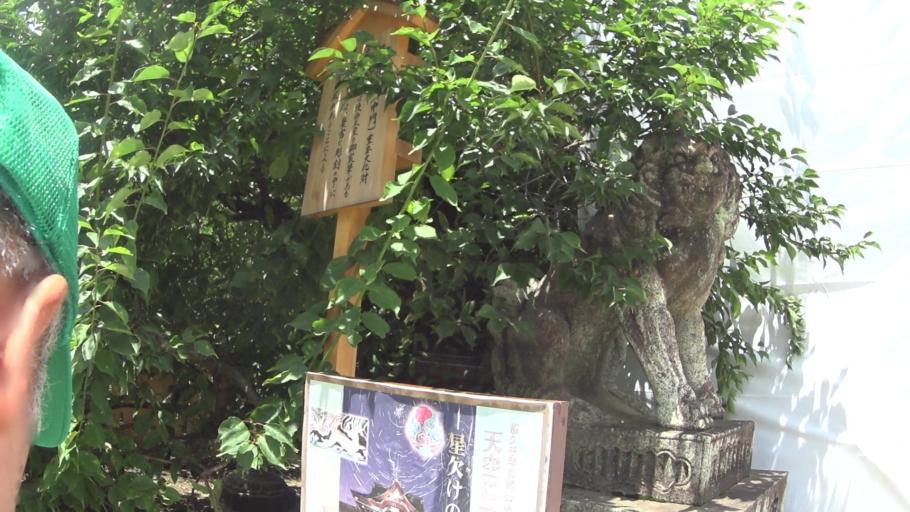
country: JP
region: Kyoto
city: Kyoto
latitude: 35.0308
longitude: 135.7351
